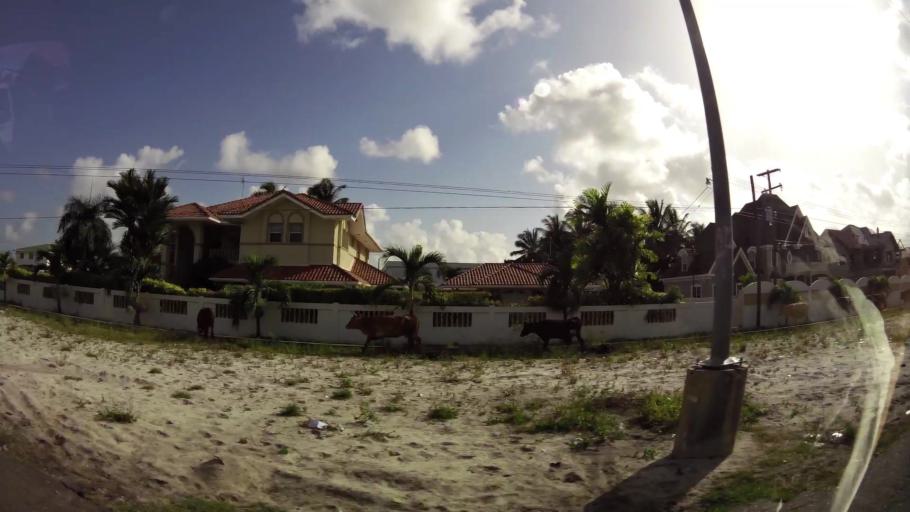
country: GY
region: Demerara-Mahaica
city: Georgetown
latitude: 6.8169
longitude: -58.0756
